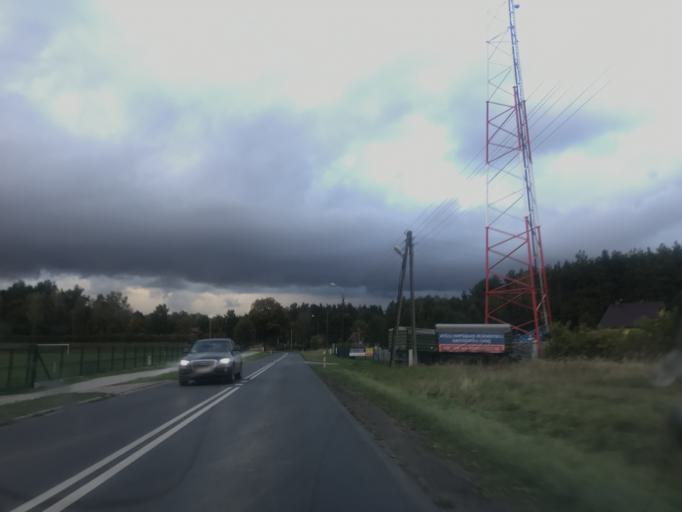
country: PL
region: West Pomeranian Voivodeship
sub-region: Powiat walecki
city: Tuczno
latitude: 53.2039
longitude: 16.1646
